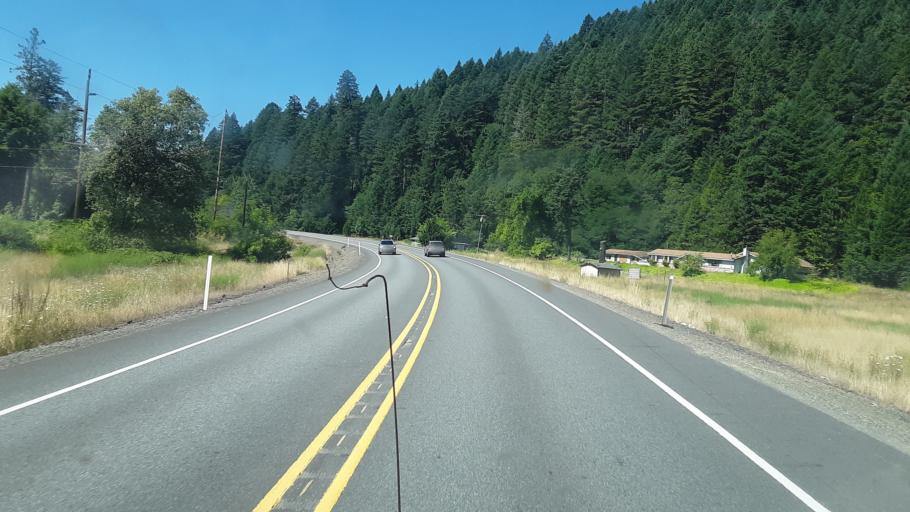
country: US
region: Oregon
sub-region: Josephine County
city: Redwood
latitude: 42.3767
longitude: -123.4976
